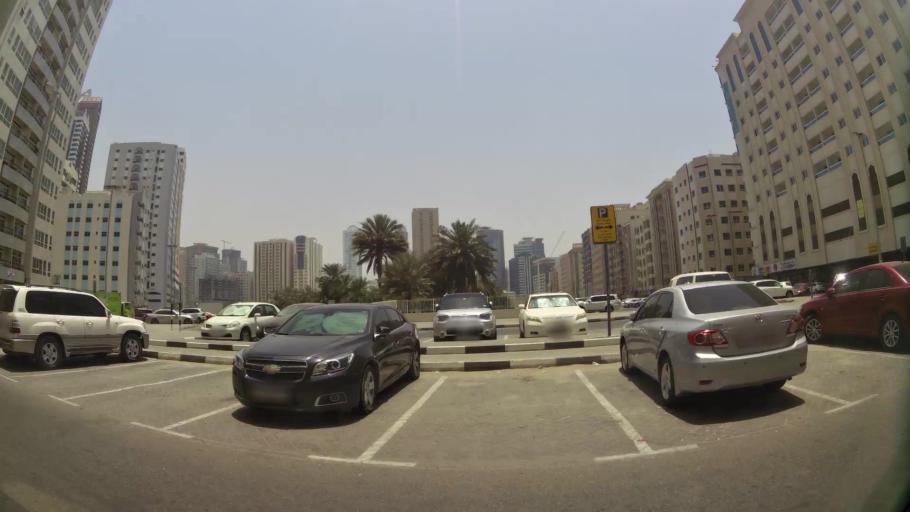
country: AE
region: Ash Shariqah
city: Sharjah
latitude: 25.3357
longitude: 55.3738
